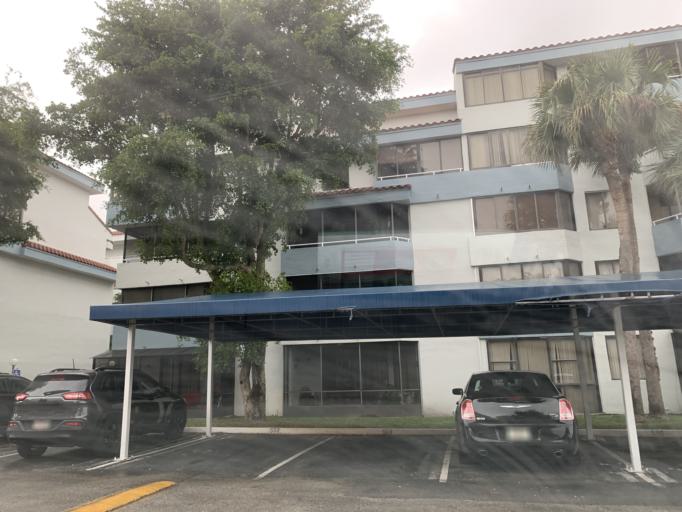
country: US
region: Florida
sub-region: Miami-Dade County
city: Kendall West
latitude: 25.6887
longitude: -80.4390
